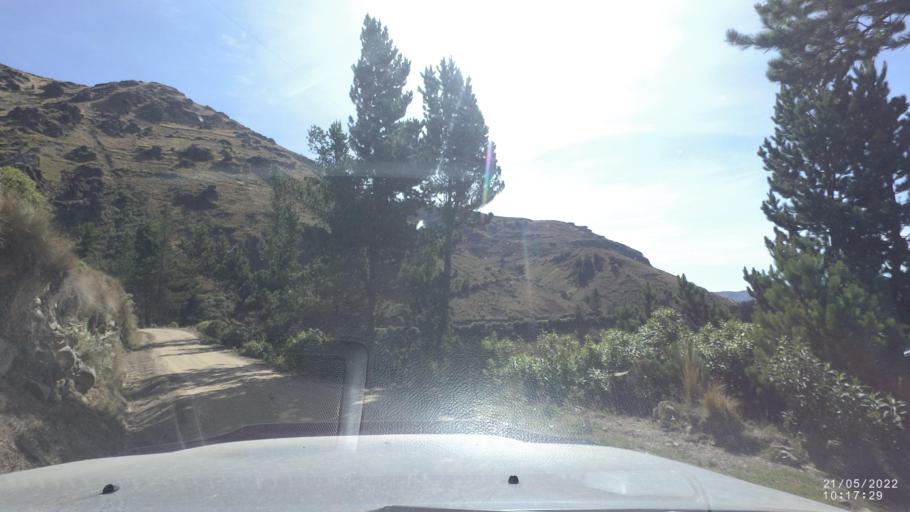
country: BO
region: Cochabamba
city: Colomi
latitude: -17.3292
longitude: -65.9630
